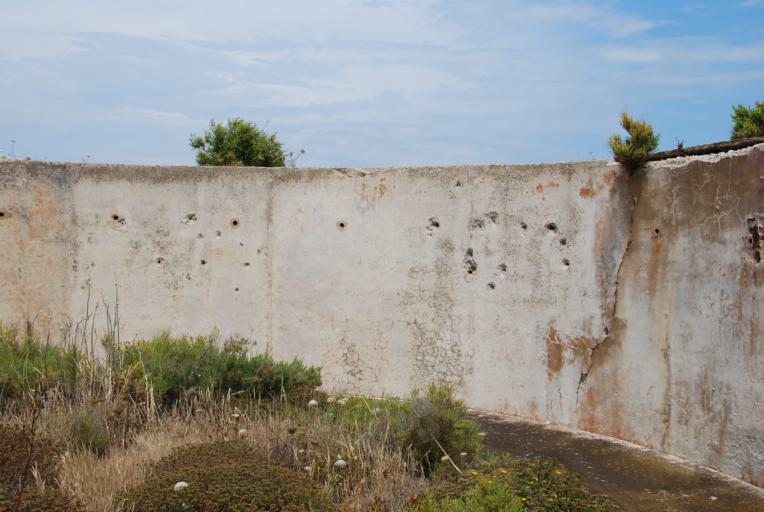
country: ES
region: Balearic Islands
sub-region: Illes Balears
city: Es Castell
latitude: 39.8783
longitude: 4.3212
